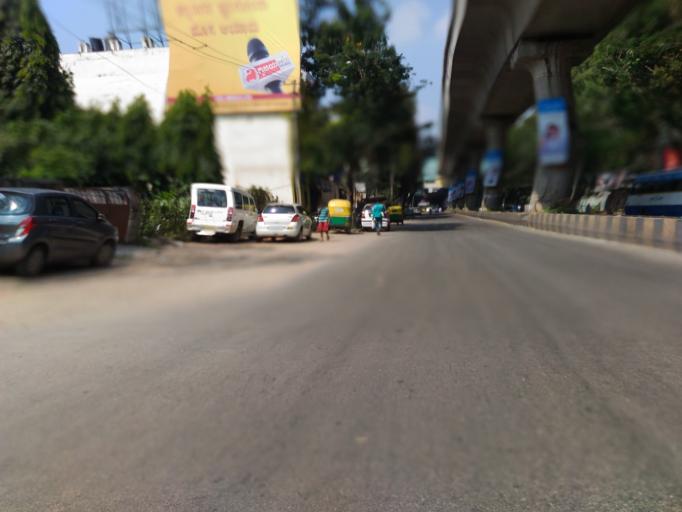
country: IN
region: Karnataka
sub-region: Bangalore Urban
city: Bangalore
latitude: 12.9441
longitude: 77.5800
